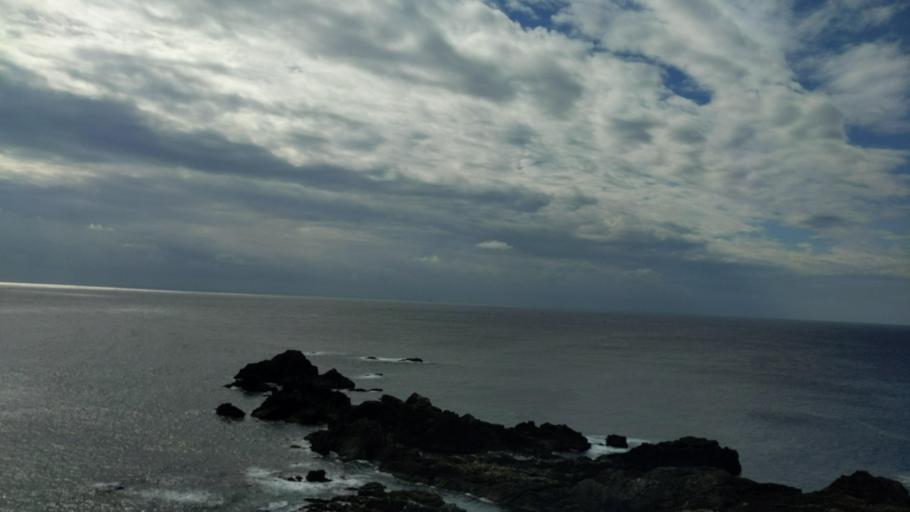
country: JP
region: Wakayama
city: Shingu
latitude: 33.4376
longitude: 135.7544
